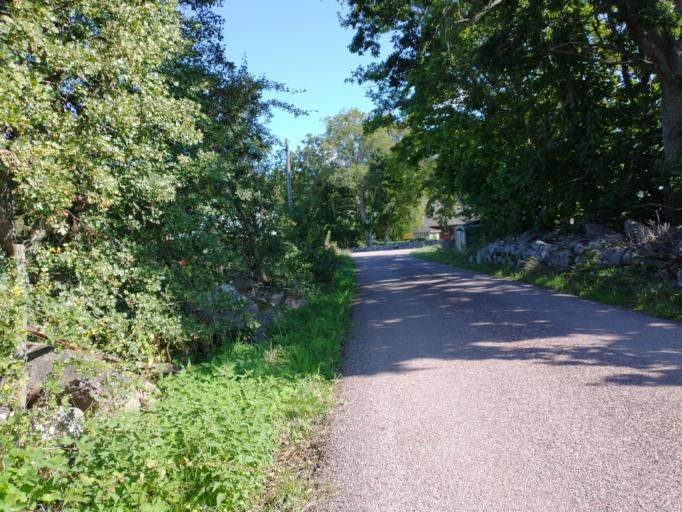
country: SE
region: Kalmar
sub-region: Kalmar Kommun
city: Lindsdal
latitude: 56.7962
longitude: 16.2672
